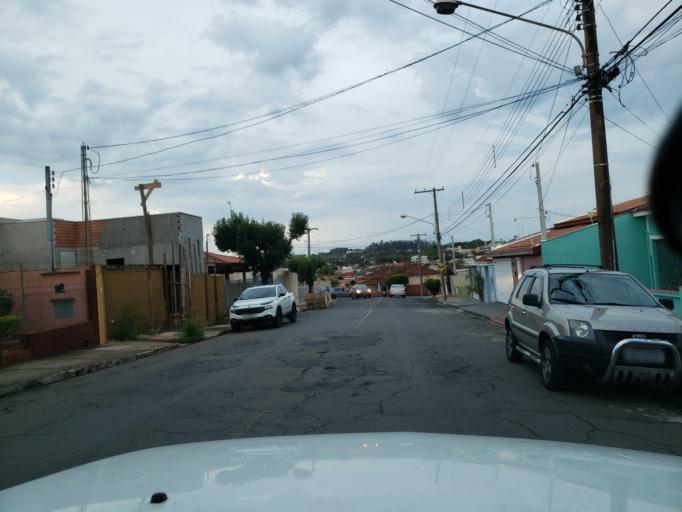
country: BR
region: Sao Paulo
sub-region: Moji-Guacu
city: Mogi-Gaucu
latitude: -22.3631
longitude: -46.9412
